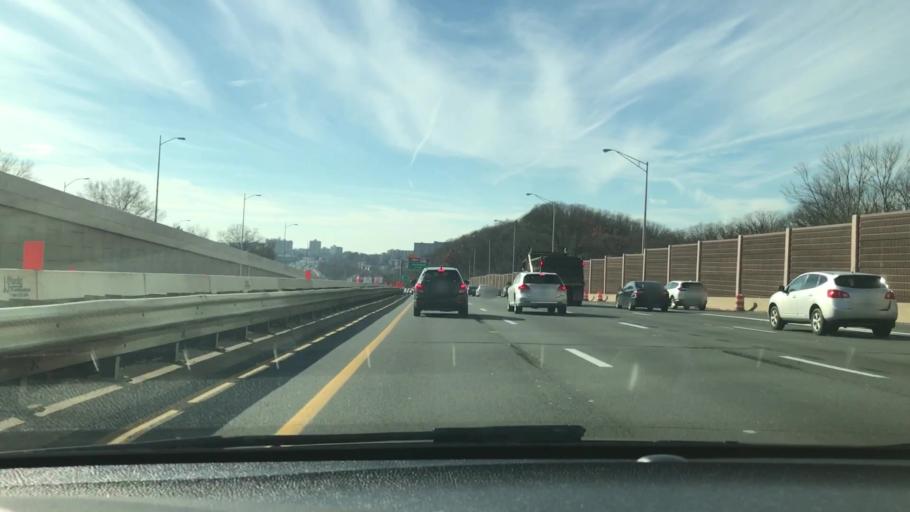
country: US
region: Virginia
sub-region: Fairfax County
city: Baileys Crossroads
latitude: 38.8287
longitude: -77.1179
